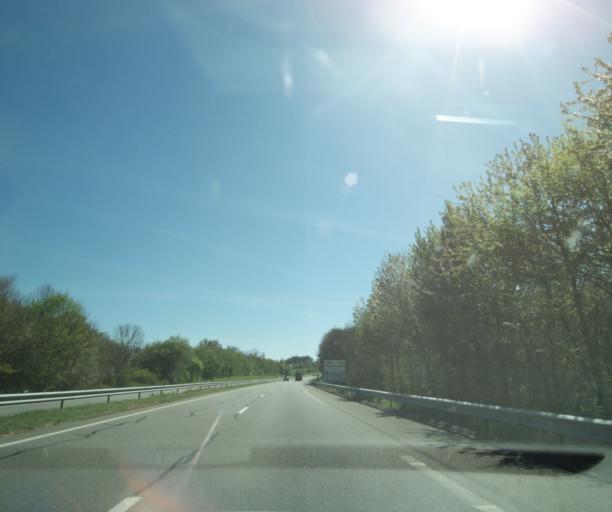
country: FR
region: Limousin
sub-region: Departement de la Correze
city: Uzerche
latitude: 45.4905
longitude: 1.5279
